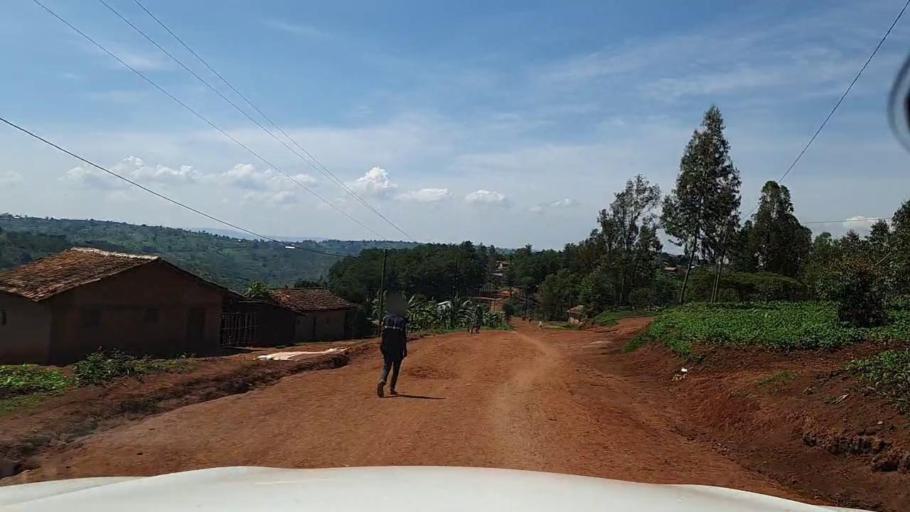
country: RW
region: Southern Province
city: Butare
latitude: -2.7139
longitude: 29.8397
